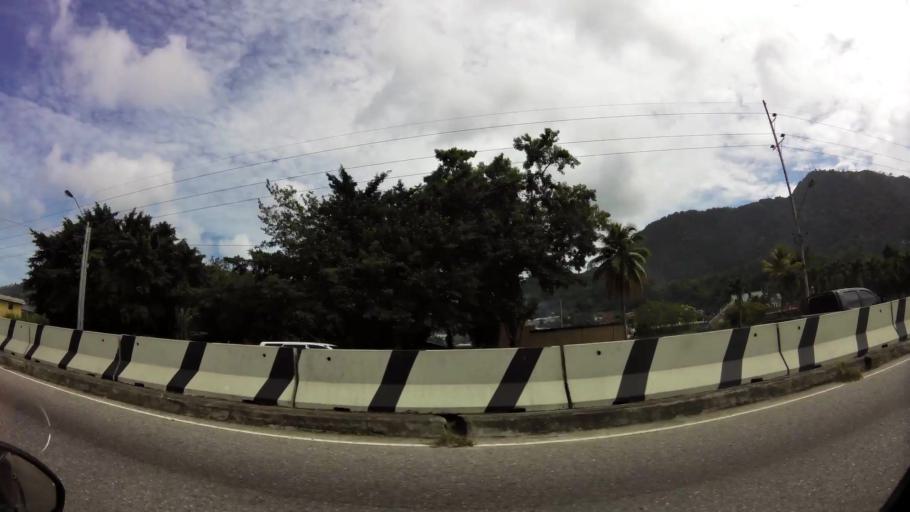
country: TT
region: Diego Martin
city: Petit Valley
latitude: 10.7047
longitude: -61.5538
